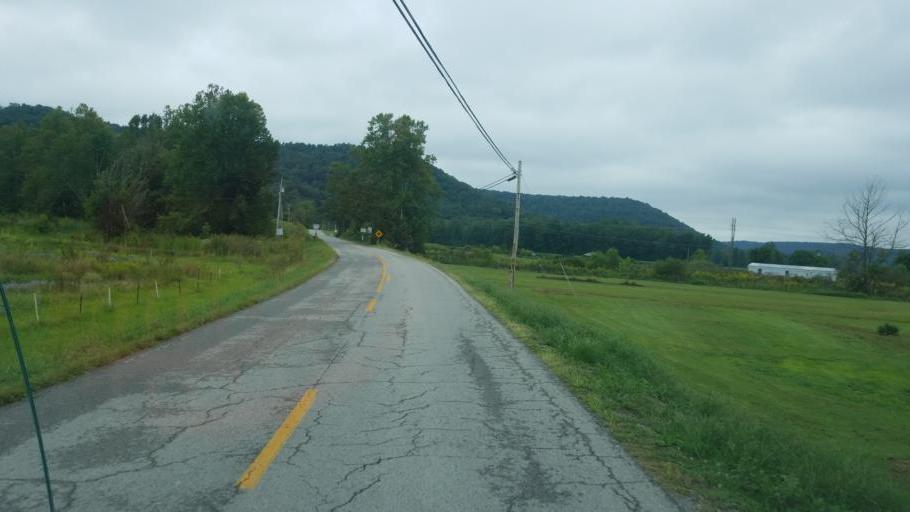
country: US
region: Kentucky
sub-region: Rowan County
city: Morehead
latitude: 38.3215
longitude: -83.5505
